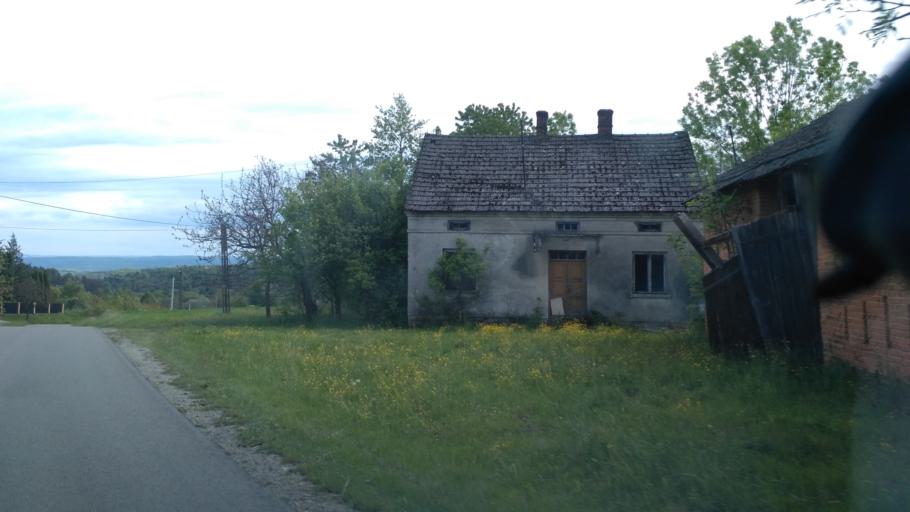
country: PL
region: Subcarpathian Voivodeship
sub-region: Powiat przemyski
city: Nienadowa
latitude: 49.8789
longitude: 22.4173
